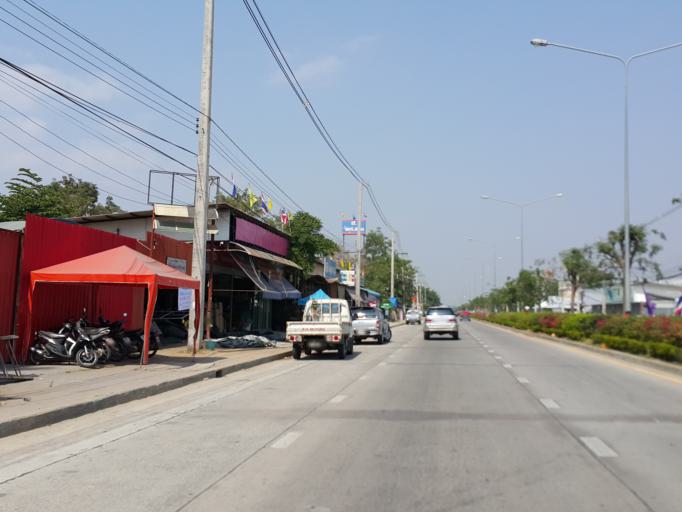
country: TH
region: Chiang Mai
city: Chiang Mai
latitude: 18.7868
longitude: 99.0410
